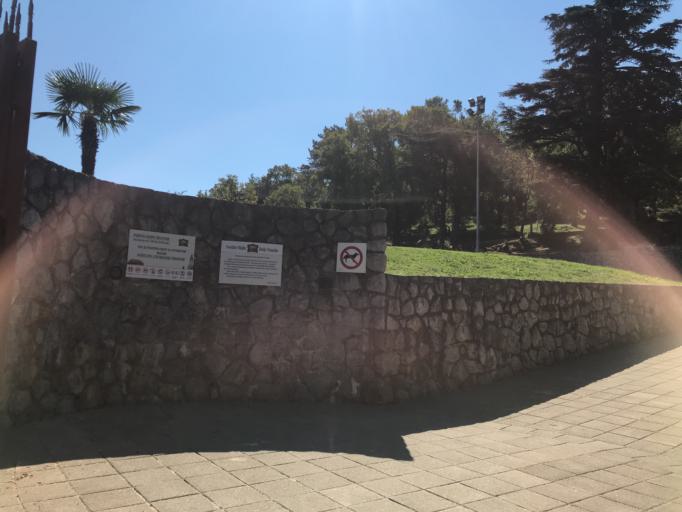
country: HR
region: Primorsko-Goranska
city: Drenova
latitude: 45.3307
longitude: 14.4566
